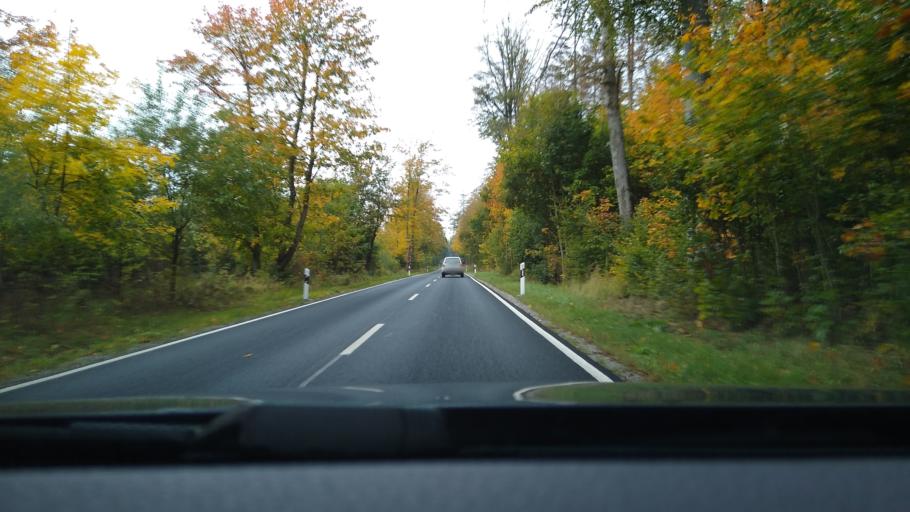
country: DE
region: Saxony-Anhalt
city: Elbingerode
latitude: 51.7731
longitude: 10.7861
